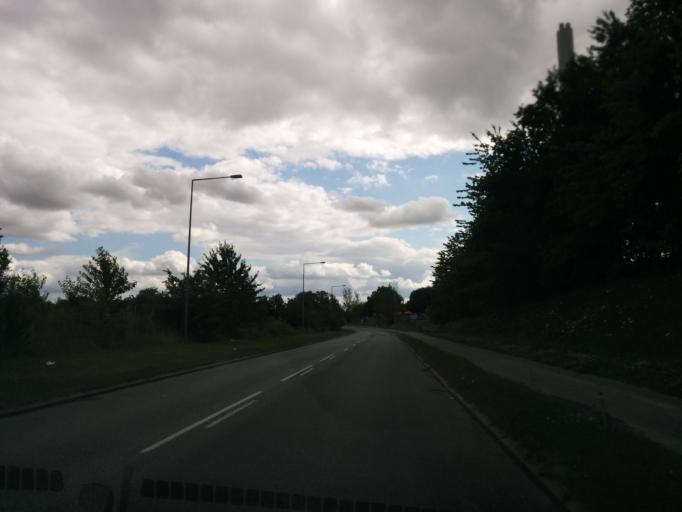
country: DK
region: Central Jutland
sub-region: Arhus Kommune
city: Tranbjerg
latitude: 56.1090
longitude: 10.1034
